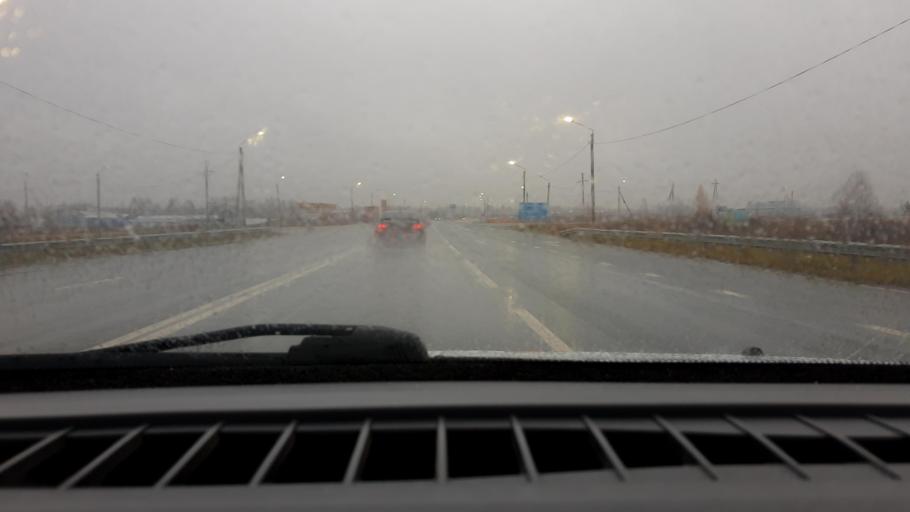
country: RU
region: Nizjnij Novgorod
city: Sitniki
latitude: 56.5034
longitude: 44.0245
